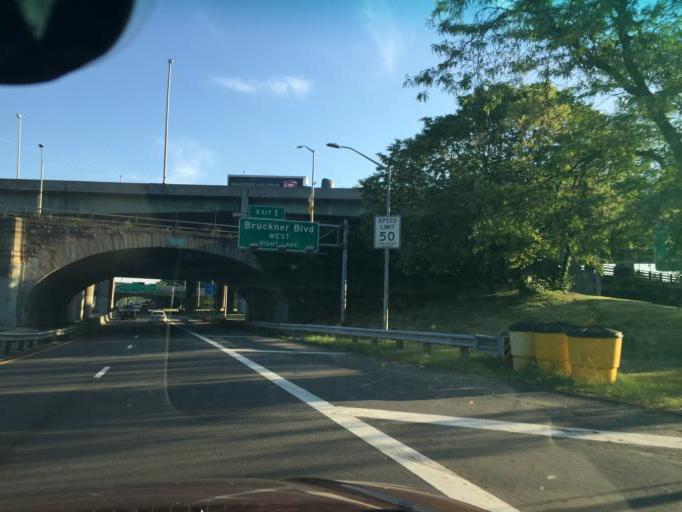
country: US
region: New York
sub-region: Bronx
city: The Bronx
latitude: 40.8277
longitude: -73.8366
